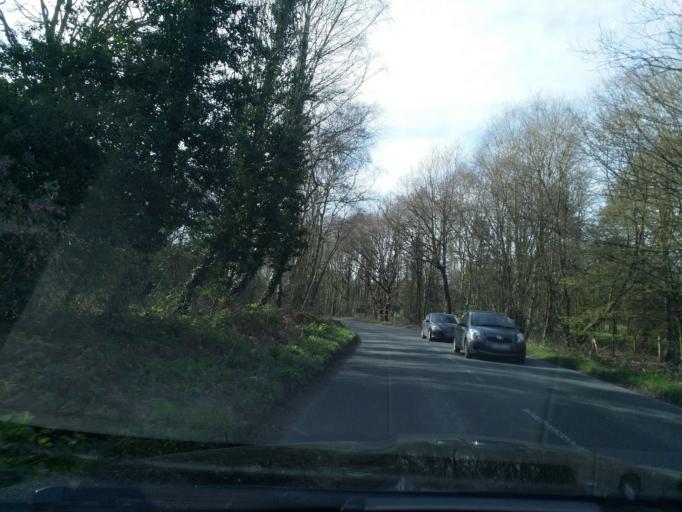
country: GB
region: England
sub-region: Hampshire
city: Farnborough
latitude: 51.2841
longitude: -0.7818
